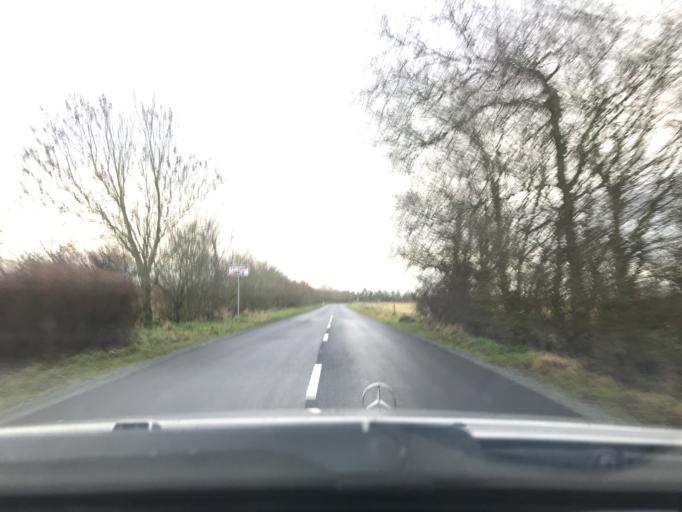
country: DK
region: South Denmark
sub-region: Esbjerg Kommune
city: Ribe
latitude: 55.3032
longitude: 8.6900
